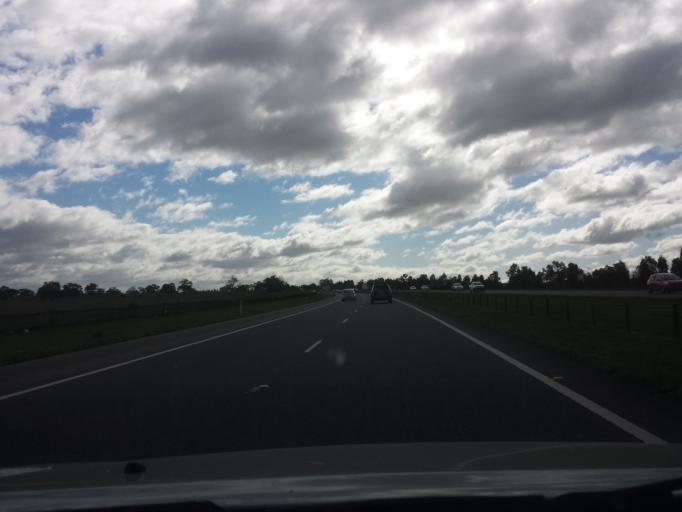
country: AU
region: Victoria
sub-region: Whittlesea
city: Epping
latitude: -37.6247
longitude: 144.9933
